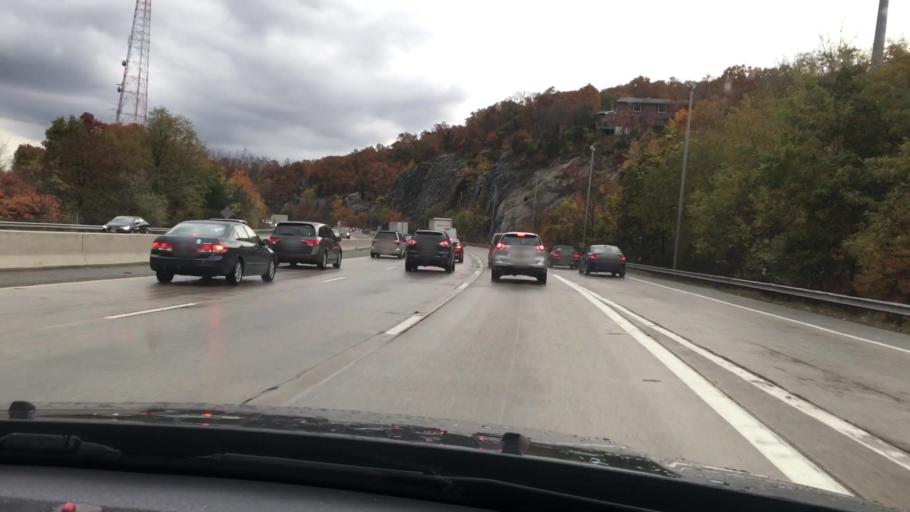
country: US
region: New Jersey
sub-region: Passaic County
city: Pompton Lakes
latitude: 41.0153
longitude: -74.2999
